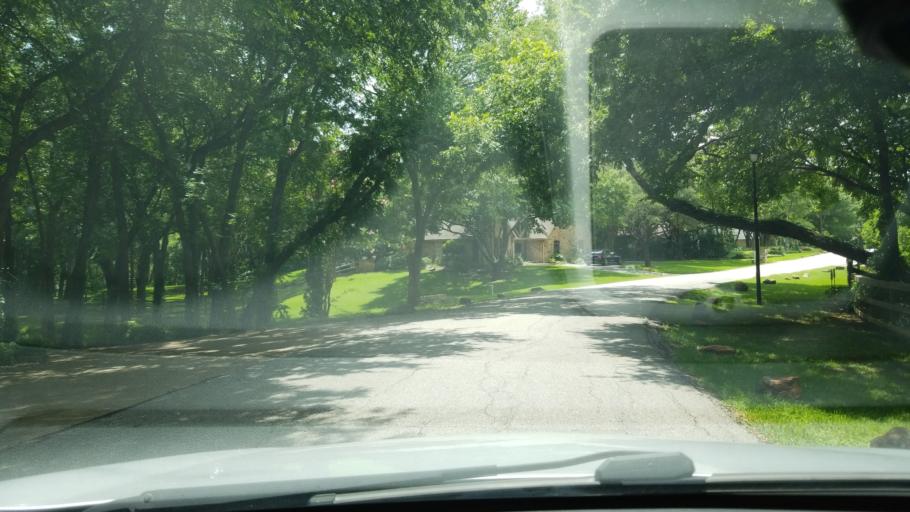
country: US
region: Texas
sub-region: Dallas County
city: Coppell
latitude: 32.9556
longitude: -96.9827
